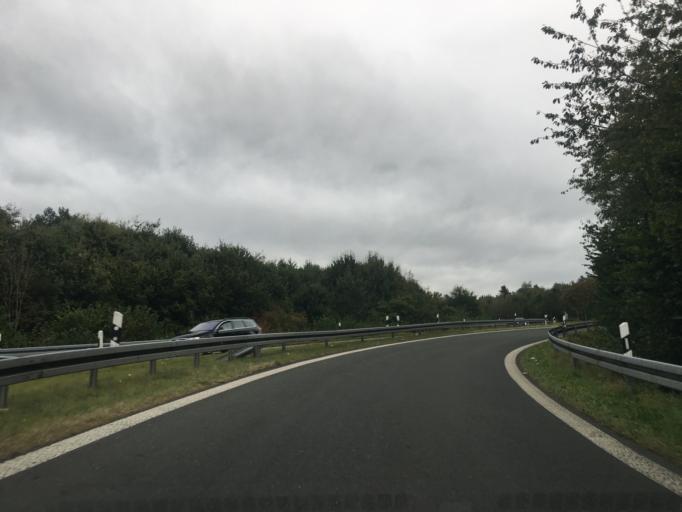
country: DE
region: North Rhine-Westphalia
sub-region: Regierungsbezirk Munster
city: Ochtrup
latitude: 52.1934
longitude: 7.1182
